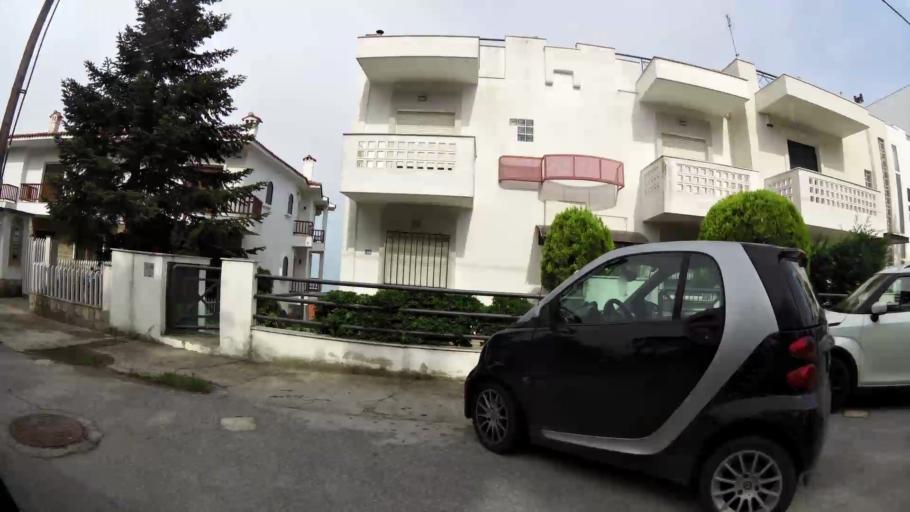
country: GR
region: Central Macedonia
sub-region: Nomos Thessalonikis
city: Panorama
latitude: 40.5874
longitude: 23.0298
